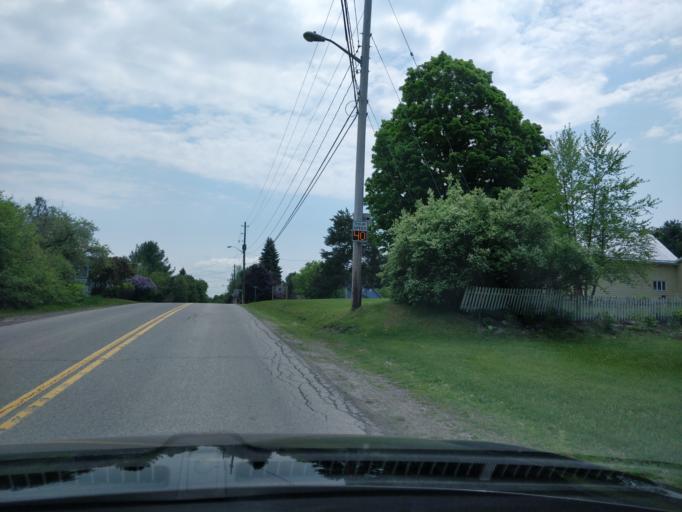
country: CA
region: Ontario
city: Perth
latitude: 44.6838
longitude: -76.4087
